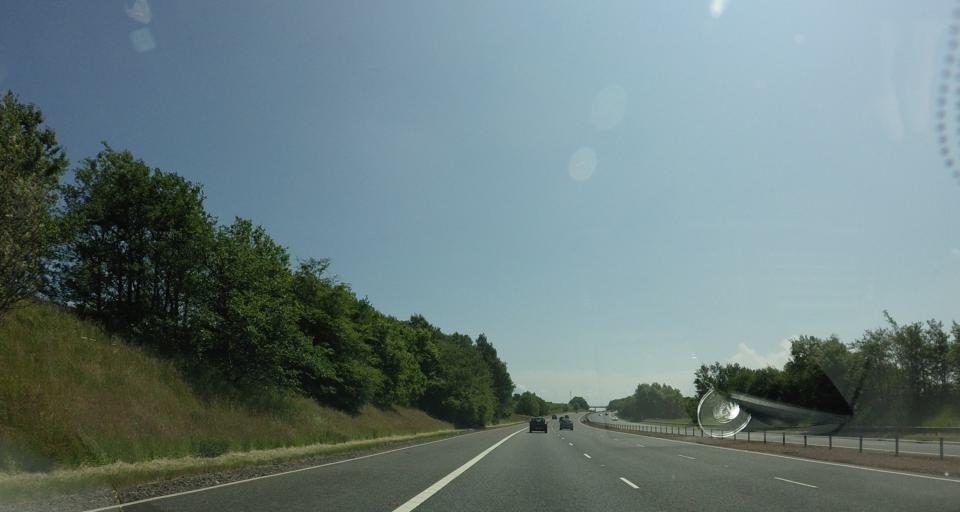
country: GB
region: Scotland
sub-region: Dumfries and Galloway
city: Annan
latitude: 55.0404
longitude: -3.1789
